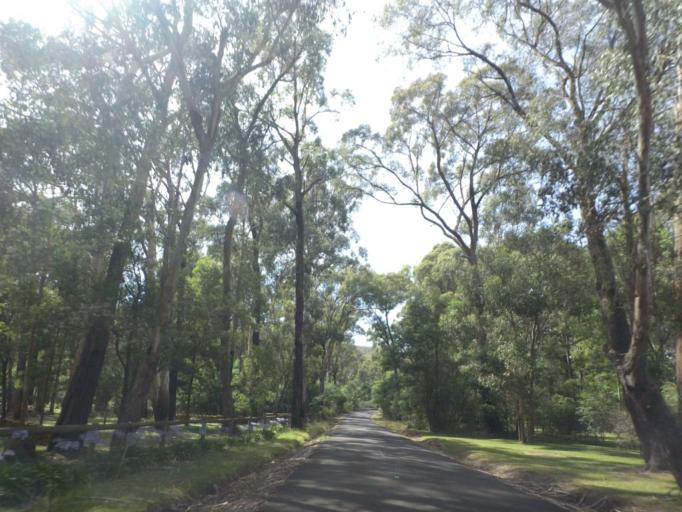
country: AU
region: Victoria
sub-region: Murrindindi
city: Kinglake West
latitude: -37.4605
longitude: 145.4201
